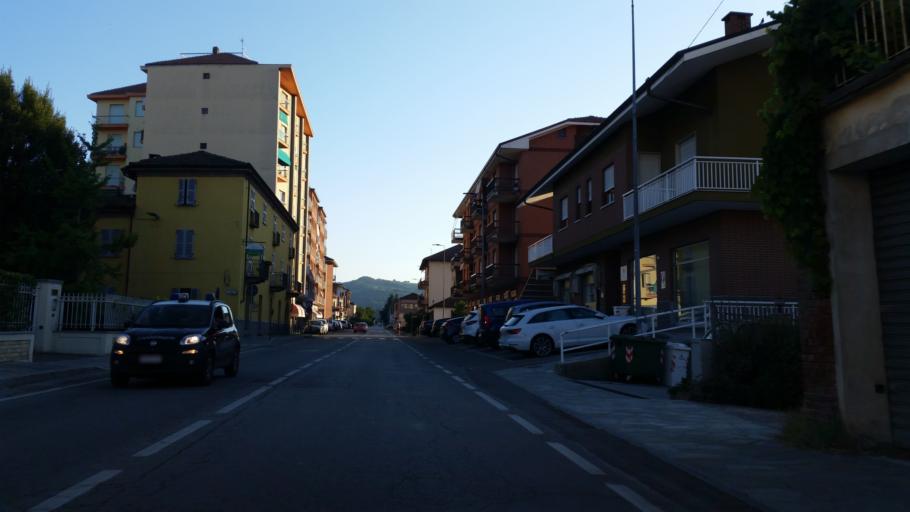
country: IT
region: Piedmont
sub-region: Provincia di Cuneo
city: Santo Stefano Belbo
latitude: 44.7070
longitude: 8.2280
